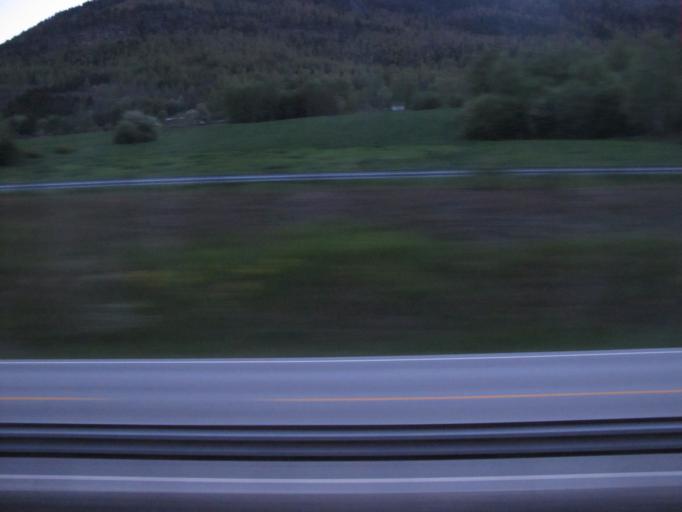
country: NO
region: Oppland
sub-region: Nord-Fron
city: Vinstra
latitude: 61.6657
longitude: 9.7174
